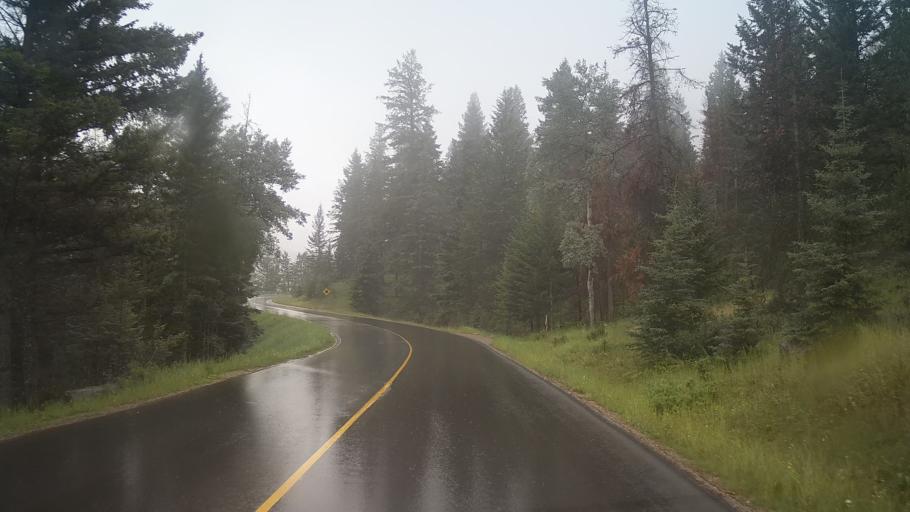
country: CA
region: Alberta
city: Jasper Park Lodge
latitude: 52.8903
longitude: -118.0814
